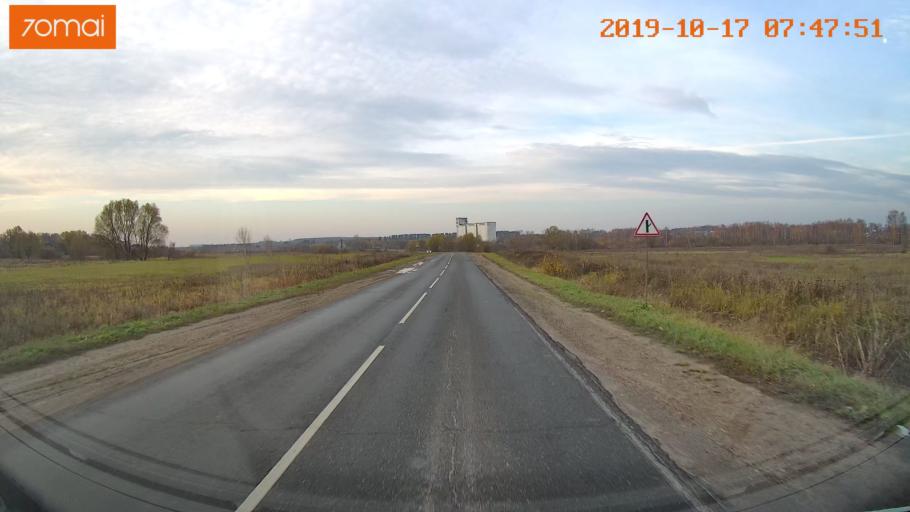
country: RU
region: Vladimir
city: Yur'yev-Pol'skiy
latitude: 56.4854
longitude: 39.6802
